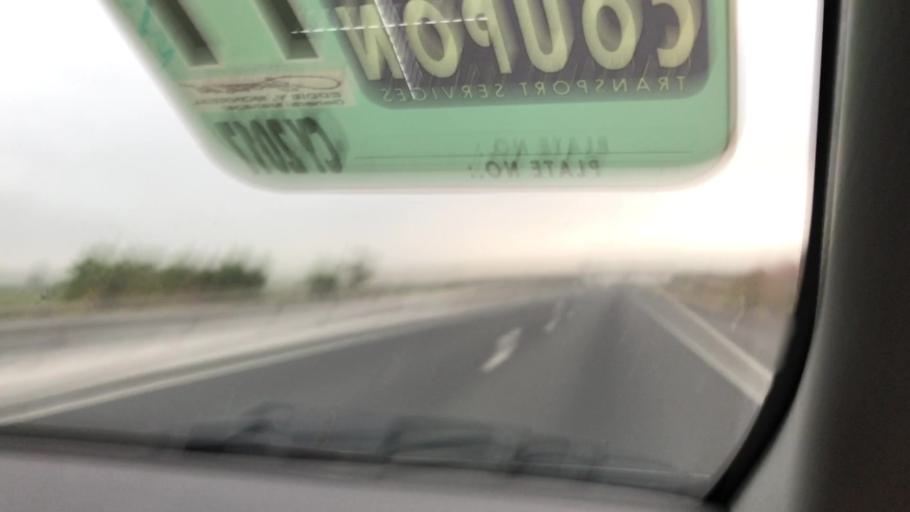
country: PH
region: Central Luzon
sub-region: Province of Tarlac
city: Mabilog
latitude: 15.4008
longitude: 120.6593
